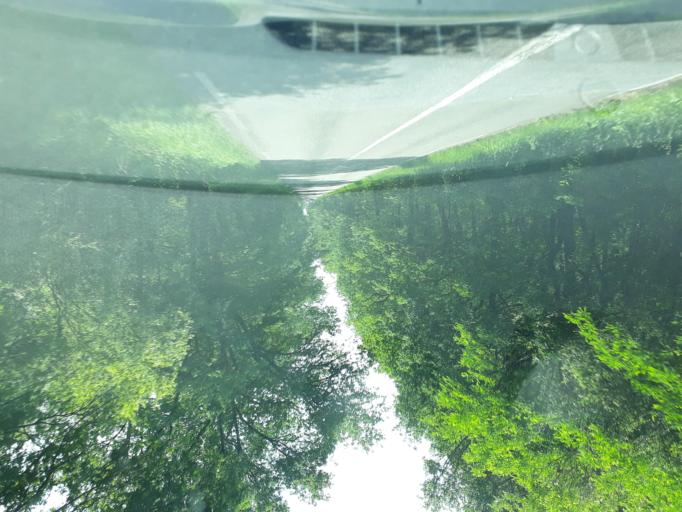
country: FR
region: Centre
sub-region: Departement du Loiret
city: Ferolles
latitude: 47.8038
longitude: 2.0734
